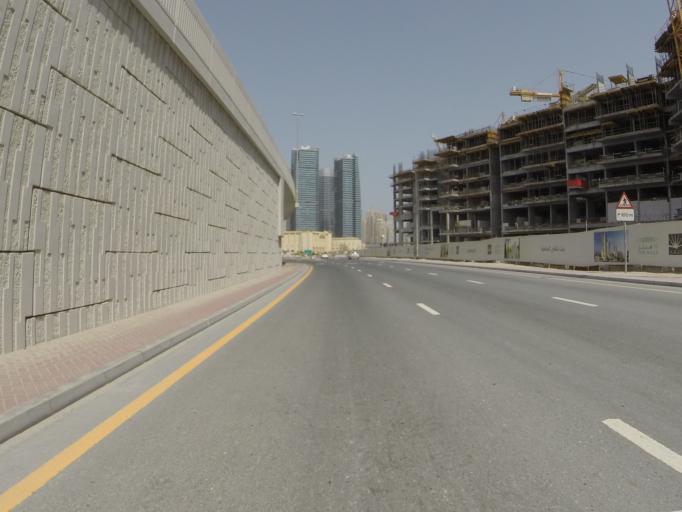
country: AE
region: Dubai
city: Dubai
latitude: 25.0772
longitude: 55.1599
